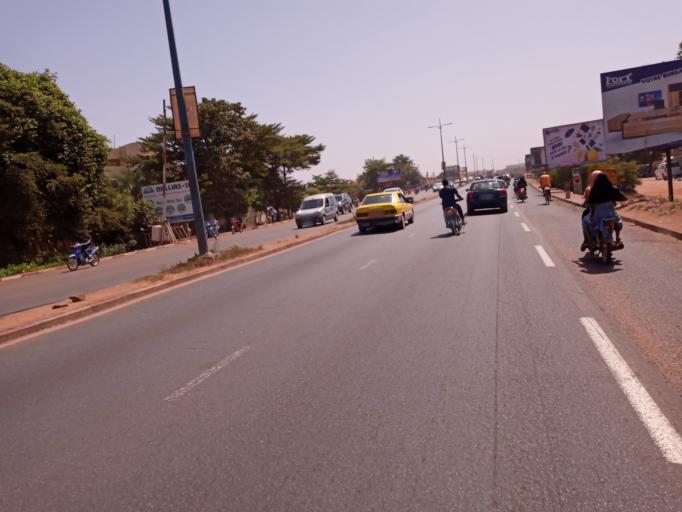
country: ML
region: Bamako
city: Bamako
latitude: 12.6172
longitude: -8.0004
